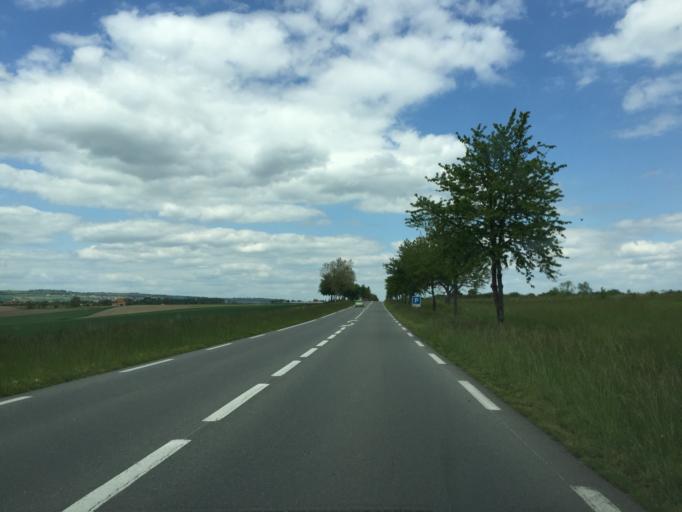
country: FR
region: Auvergne
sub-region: Departement du Puy-de-Dome
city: Aigueperse
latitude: 45.9663
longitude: 3.1775
